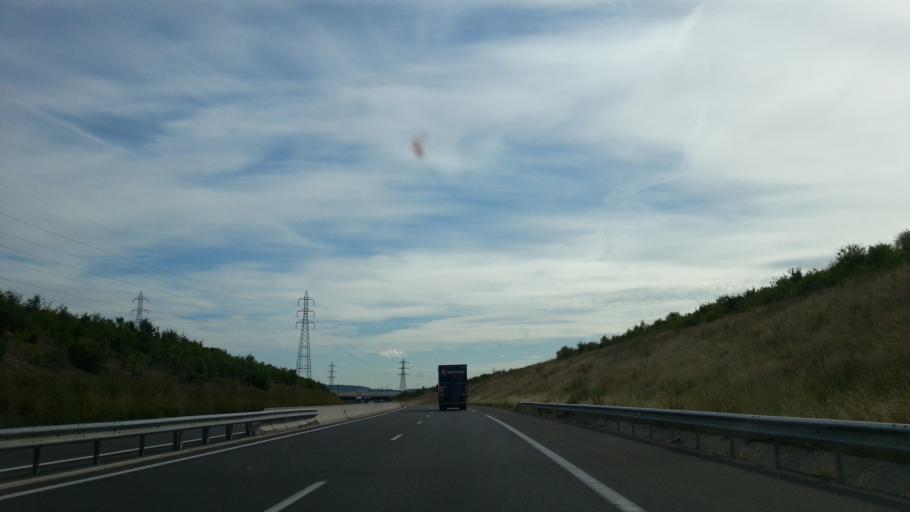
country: FR
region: Champagne-Ardenne
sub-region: Departement de la Marne
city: Cormontreuil
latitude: 49.2055
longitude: 4.0300
